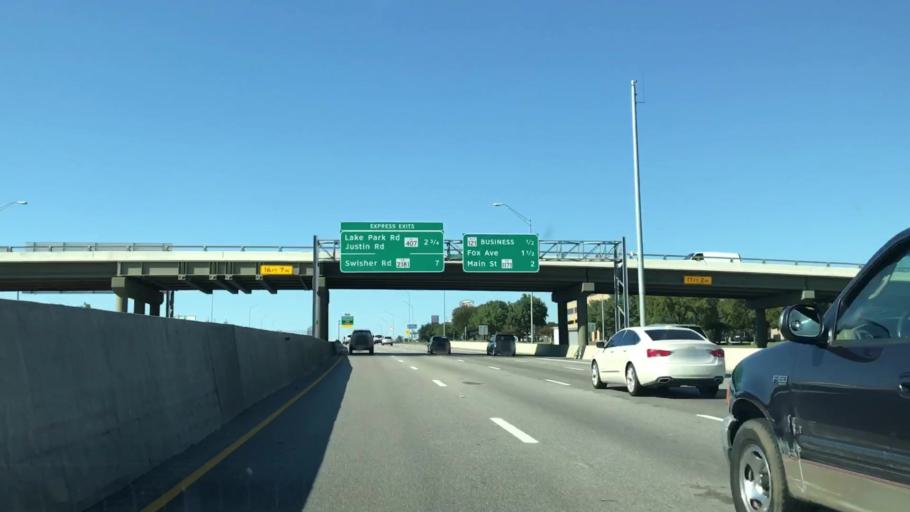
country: US
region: Texas
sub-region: Denton County
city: Lewisville
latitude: 33.0175
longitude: -96.9825
